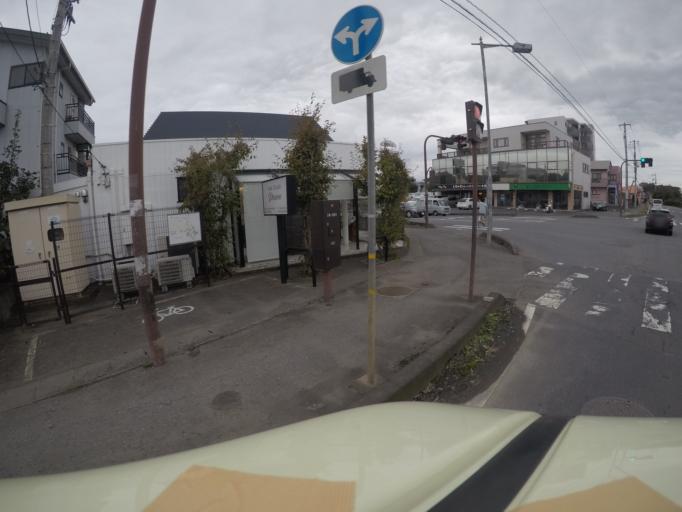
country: JP
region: Ibaraki
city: Naka
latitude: 36.1135
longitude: 140.1150
